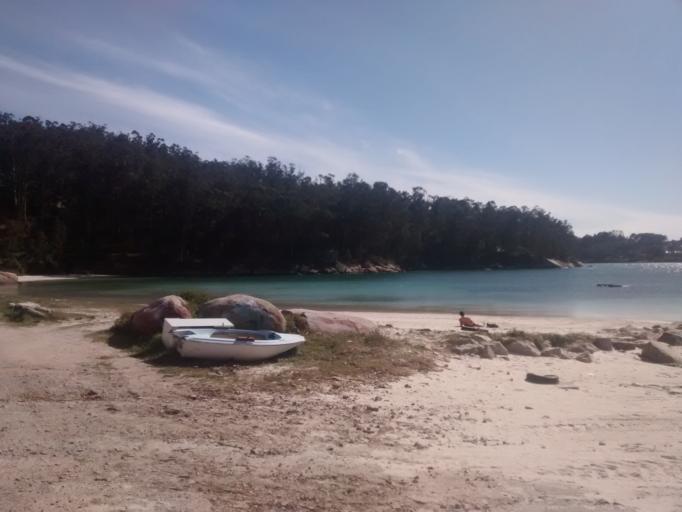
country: ES
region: Galicia
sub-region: Provincia de Pontevedra
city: O Grove
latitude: 42.4896
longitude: -8.8833
